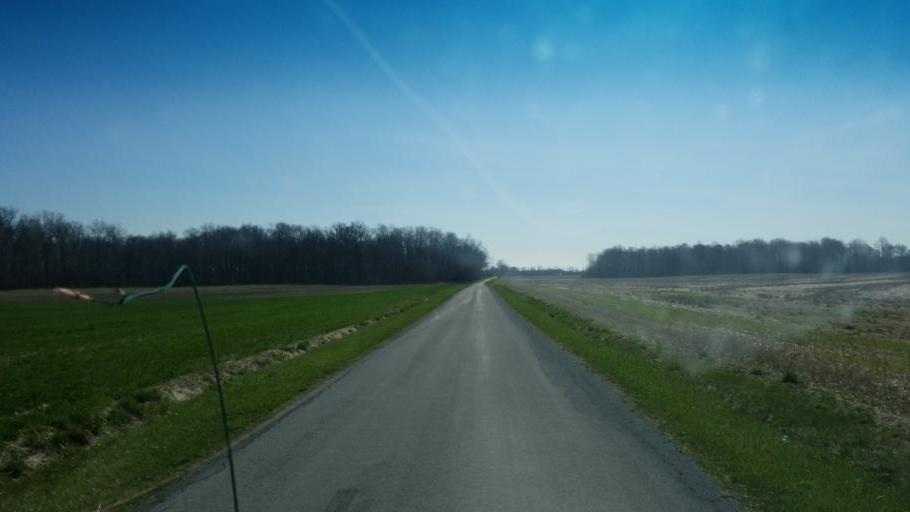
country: US
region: Ohio
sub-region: Hardin County
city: Forest
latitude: 40.7093
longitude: -83.4638
